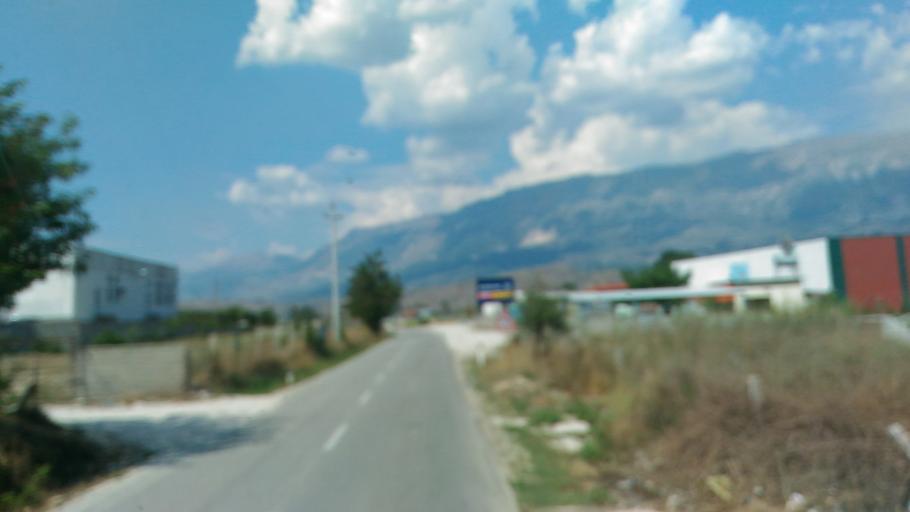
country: AL
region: Gjirokaster
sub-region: Rrethi i Gjirokastres
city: Dervician
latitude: 40.0503
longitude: 20.1773
